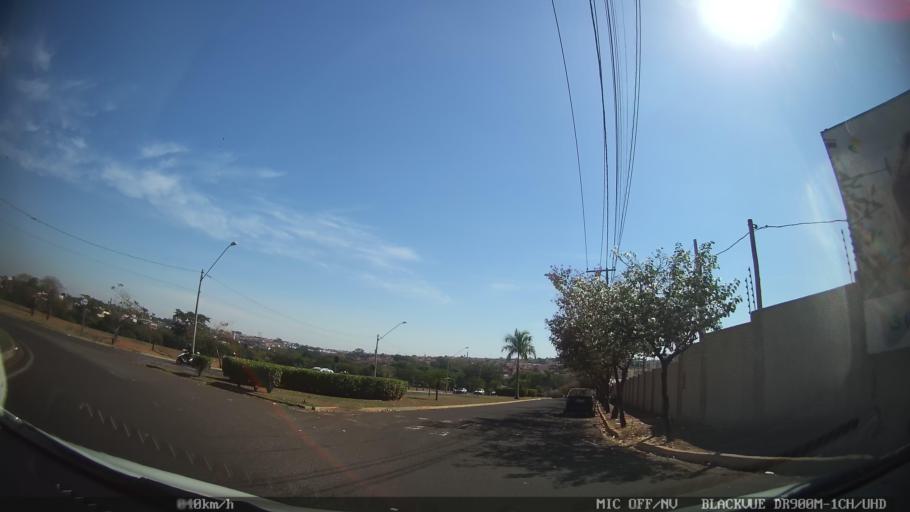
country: BR
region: Sao Paulo
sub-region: Sao Jose Do Rio Preto
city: Sao Jose do Rio Preto
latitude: -20.7788
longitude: -49.3797
